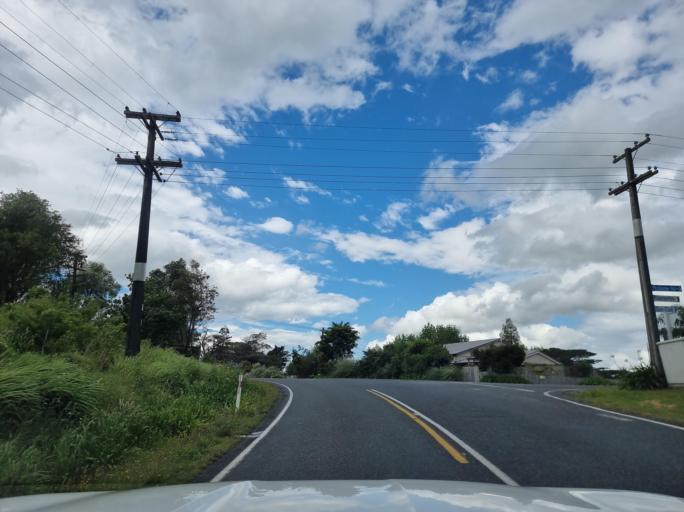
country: NZ
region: Northland
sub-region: Whangarei
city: Whangarei
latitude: -35.8464
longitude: 174.2876
